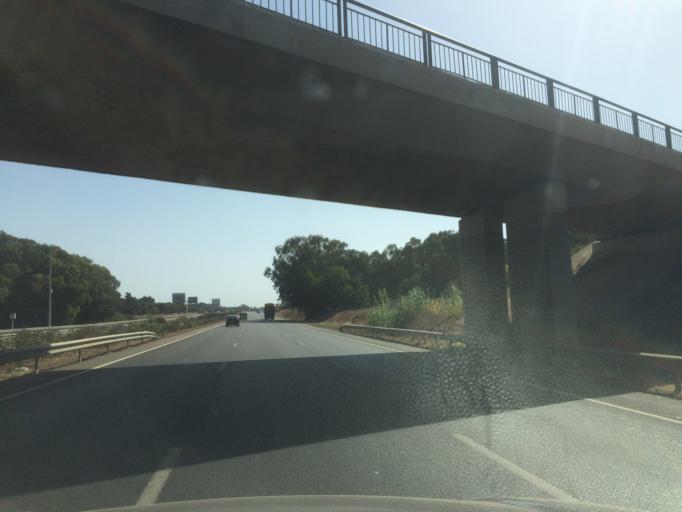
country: MA
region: Rabat-Sale-Zemmour-Zaer
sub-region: Skhirate-Temara
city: Temara
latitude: 33.9505
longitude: -6.9174
